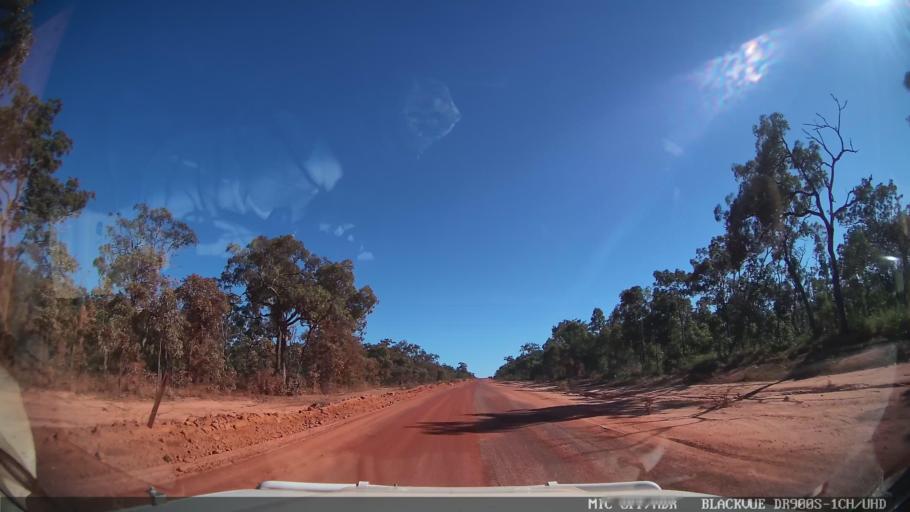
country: AU
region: Queensland
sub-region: Torres
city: Thursday Island
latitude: -11.3990
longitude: 142.3575
